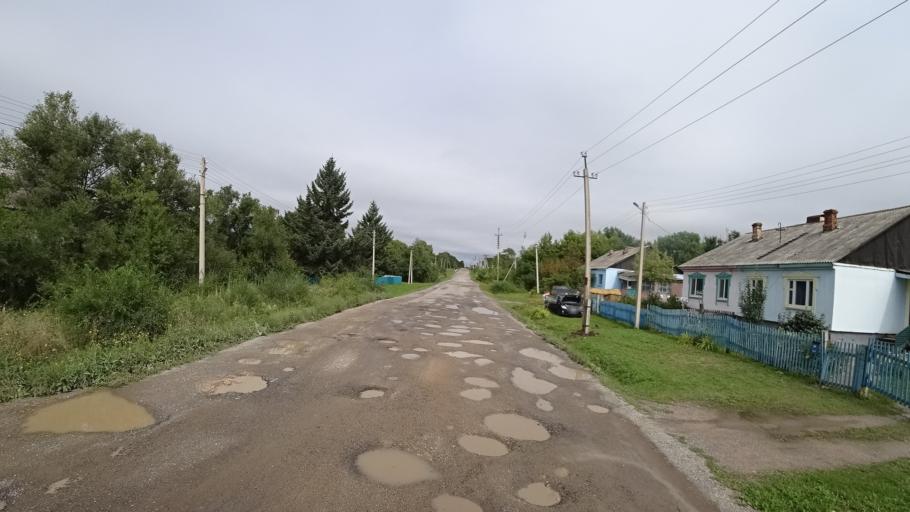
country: RU
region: Primorskiy
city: Lyalichi
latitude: 44.0755
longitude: 132.4706
